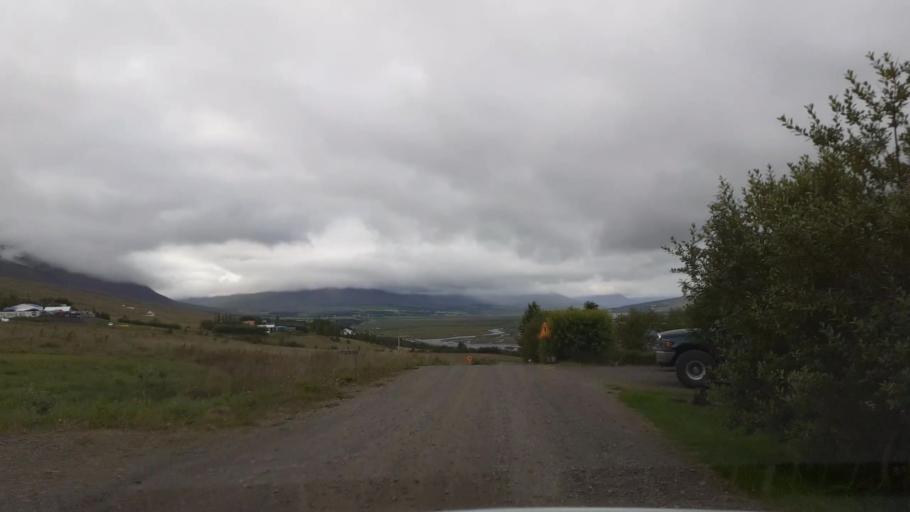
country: IS
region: Northeast
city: Akureyri
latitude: 65.6784
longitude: -18.0394
